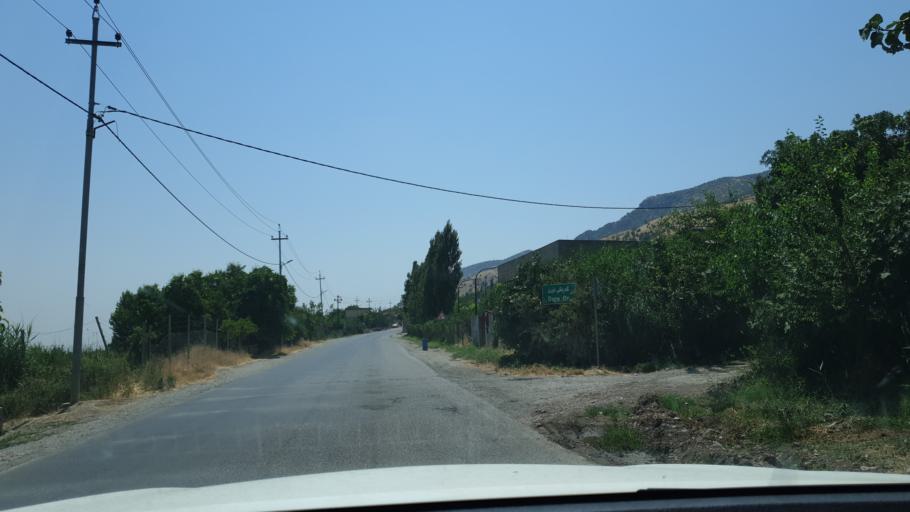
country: IQ
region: Arbil
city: Nahiyat Hiran
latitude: 36.2970
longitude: 44.4729
